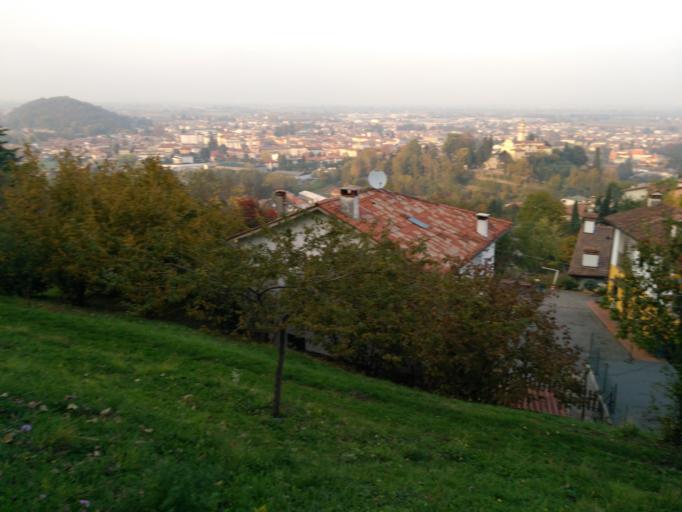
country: IT
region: Veneto
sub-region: Provincia di Vicenza
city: Malo
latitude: 45.6495
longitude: 11.4049
